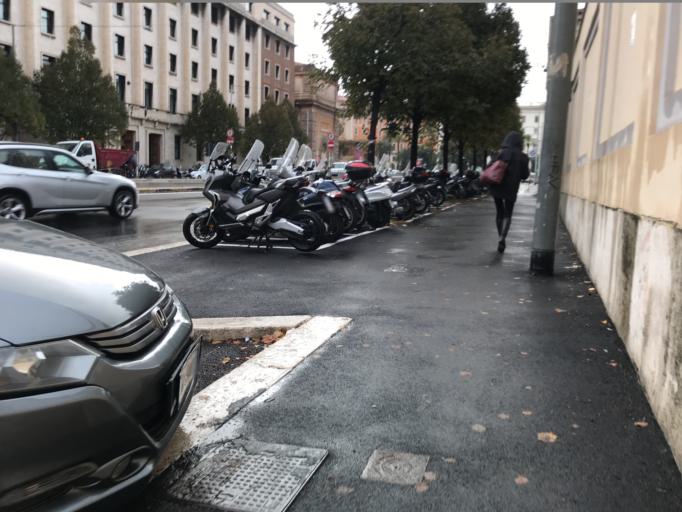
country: IT
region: Latium
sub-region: Citta metropolitana di Roma Capitale
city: Rome
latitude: 41.9069
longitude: 12.5053
